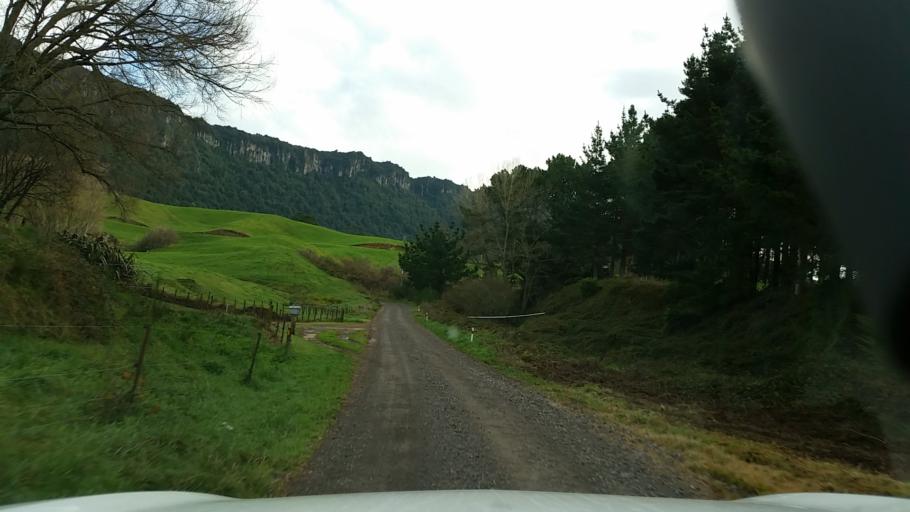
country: NZ
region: Bay of Plenty
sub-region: Rotorua District
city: Rotorua
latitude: -38.2701
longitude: 176.1562
